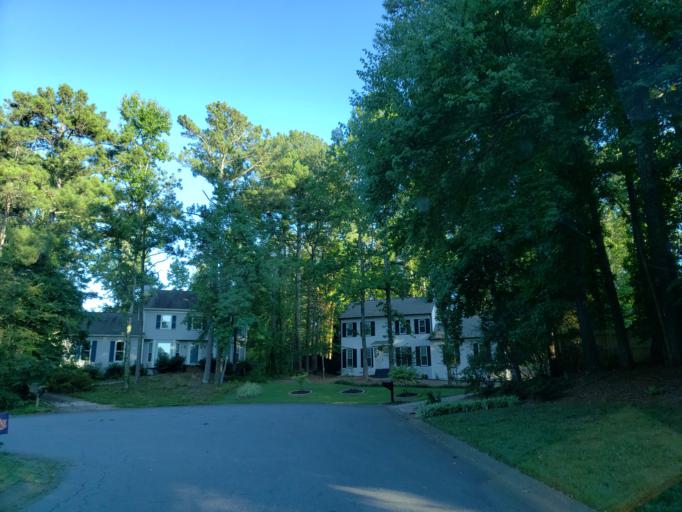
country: US
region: Georgia
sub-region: Fulton County
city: Roswell
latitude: 34.0145
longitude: -84.4608
